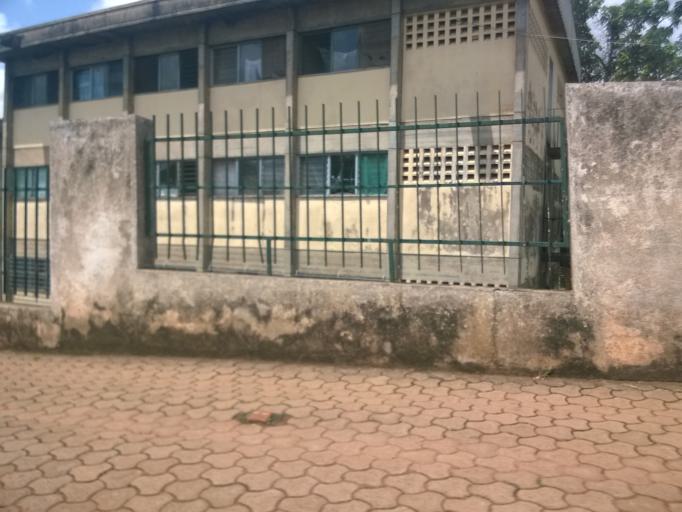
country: CM
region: Centre
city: Yaounde
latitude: 3.8612
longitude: 11.5083
